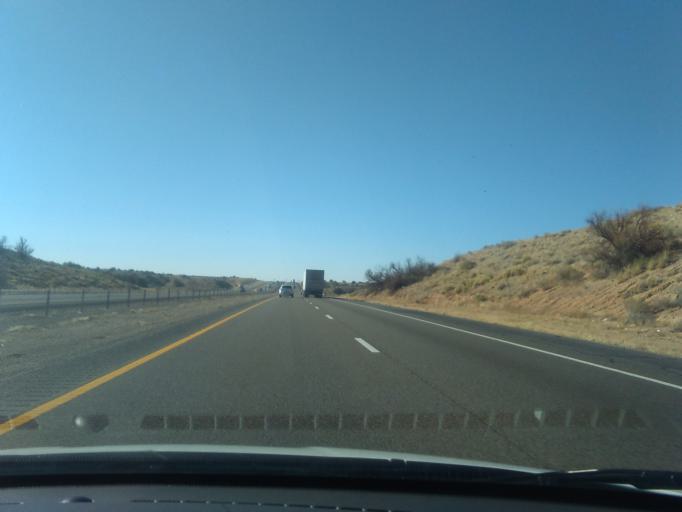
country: US
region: New Mexico
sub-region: Sandoval County
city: San Felipe Pueblo
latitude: 35.3666
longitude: -106.4844
